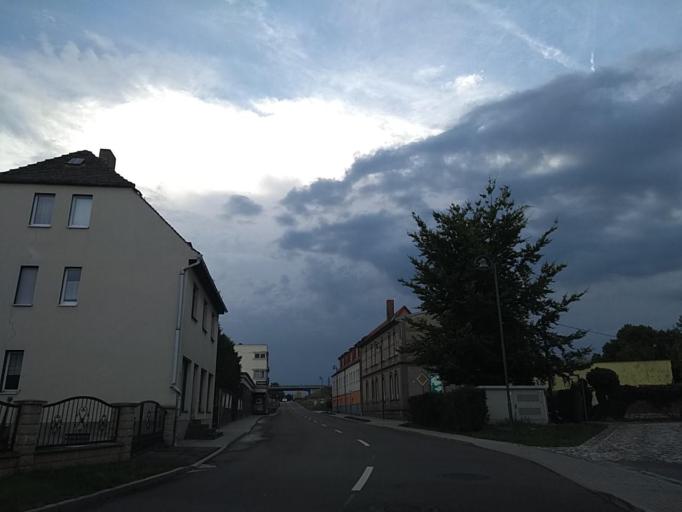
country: DE
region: Saxony-Anhalt
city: Theissen
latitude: 51.0940
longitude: 12.1171
